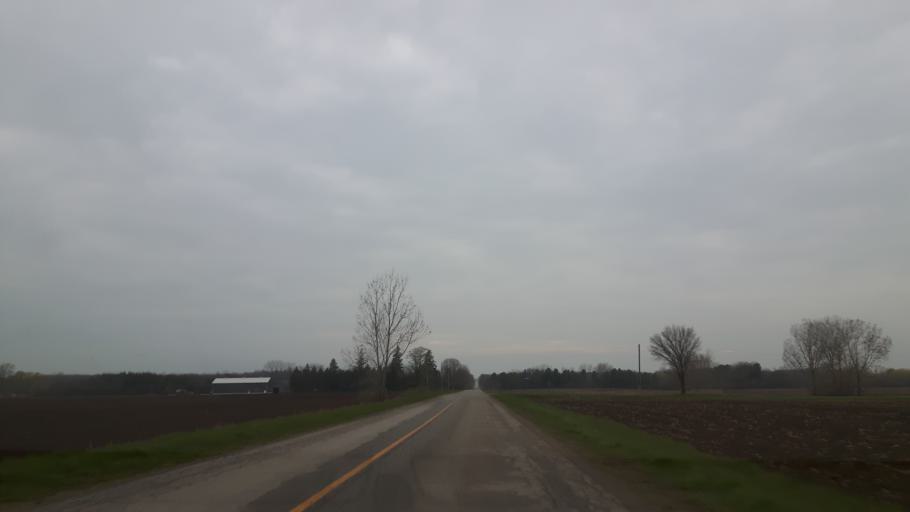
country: CA
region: Ontario
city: Bluewater
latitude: 43.5433
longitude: -81.6786
